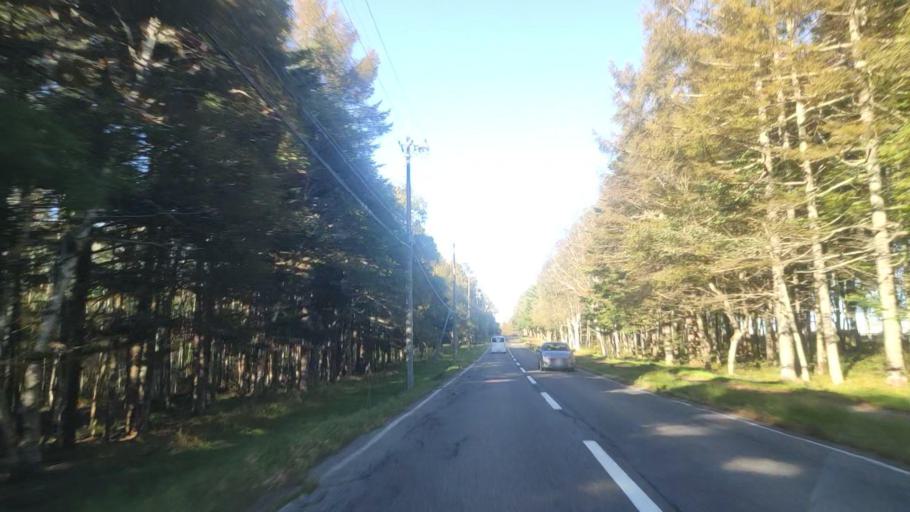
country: JP
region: Nagano
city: Kamimaruko
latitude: 36.1470
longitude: 138.2750
